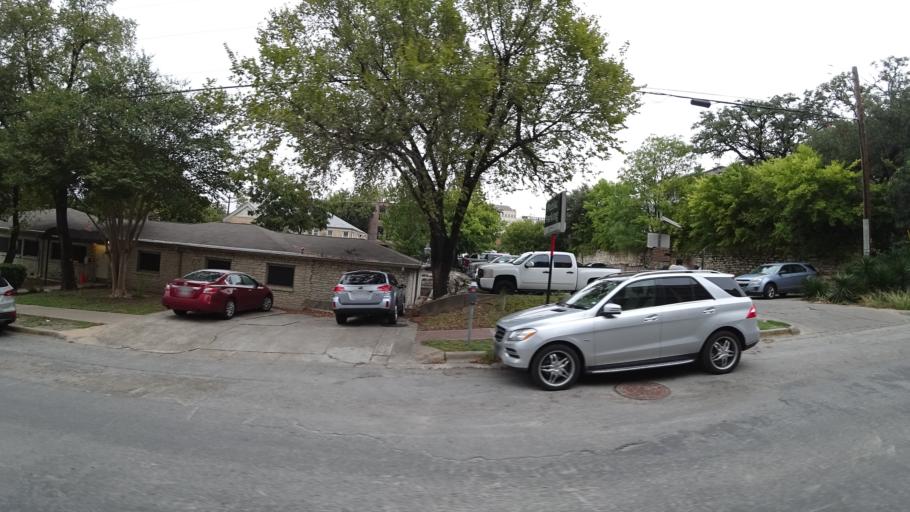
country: US
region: Texas
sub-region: Travis County
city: Austin
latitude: 30.2741
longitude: -97.7462
